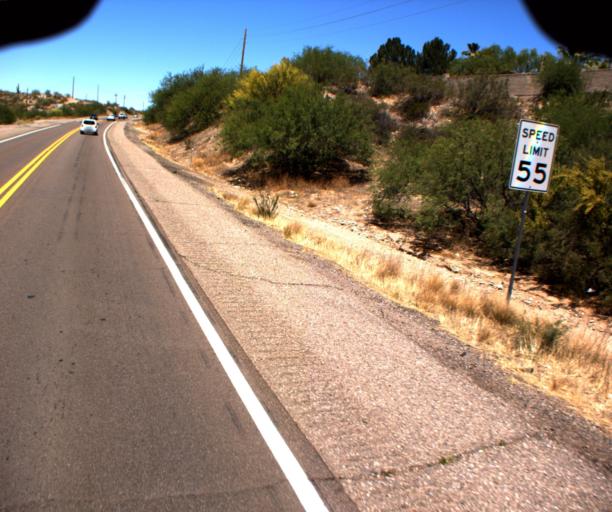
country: US
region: Arizona
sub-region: Maricopa County
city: Wickenburg
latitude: 33.9911
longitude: -112.7476
